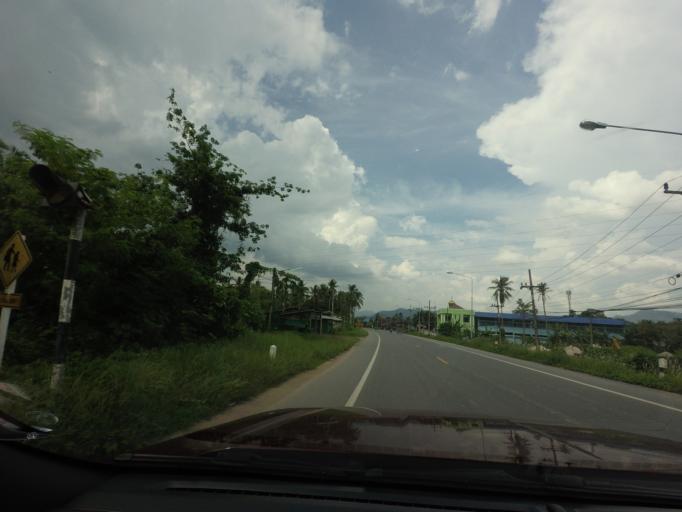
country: TH
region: Yala
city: Ban Nang Sata
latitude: 6.2581
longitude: 101.2515
